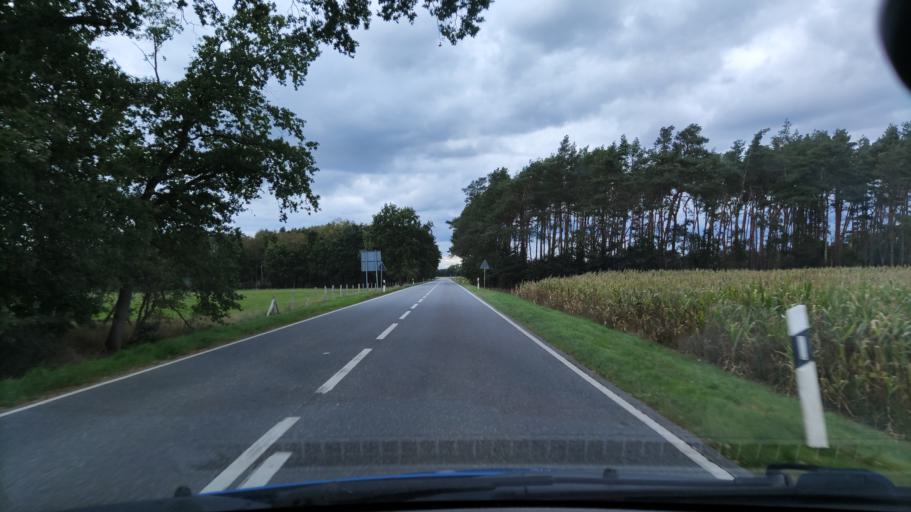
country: DE
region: Lower Saxony
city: Neu Darchau
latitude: 53.3032
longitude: 10.9690
